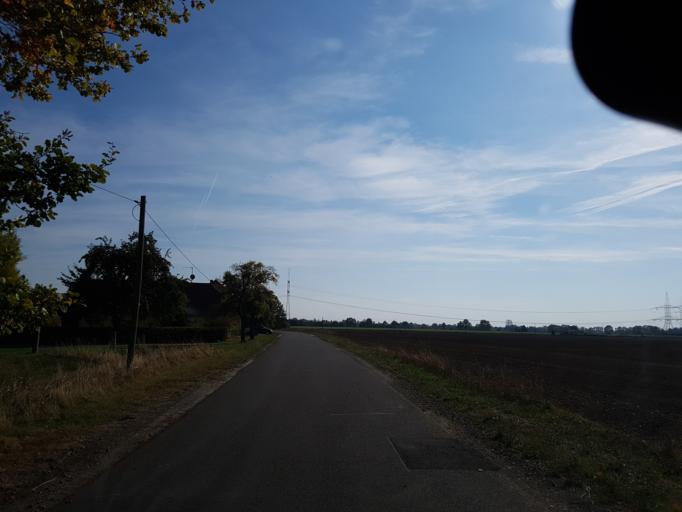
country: DE
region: Brandenburg
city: Doberlug-Kirchhain
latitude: 51.6475
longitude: 13.5444
